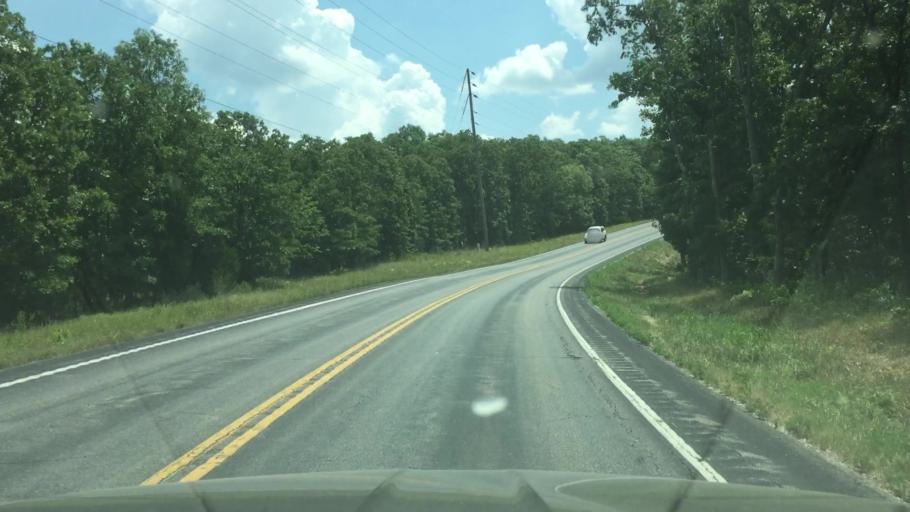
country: US
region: Missouri
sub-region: Camden County
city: Osage Beach
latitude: 38.1338
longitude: -92.5624
